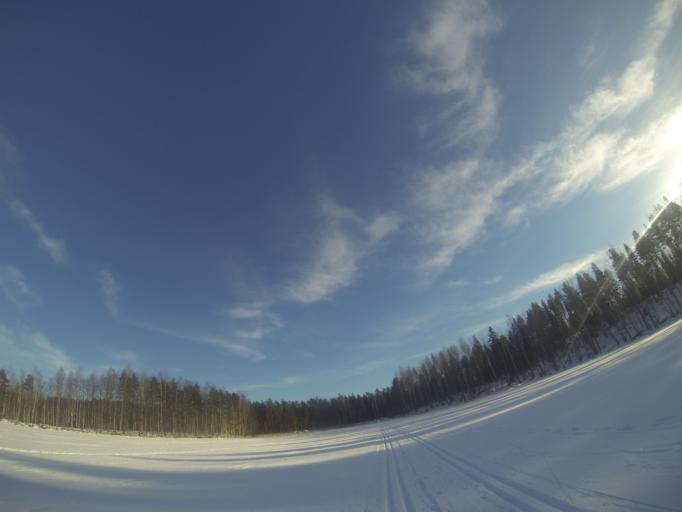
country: FI
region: Southern Savonia
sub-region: Savonlinna
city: Savonlinna
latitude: 61.8797
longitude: 28.9196
